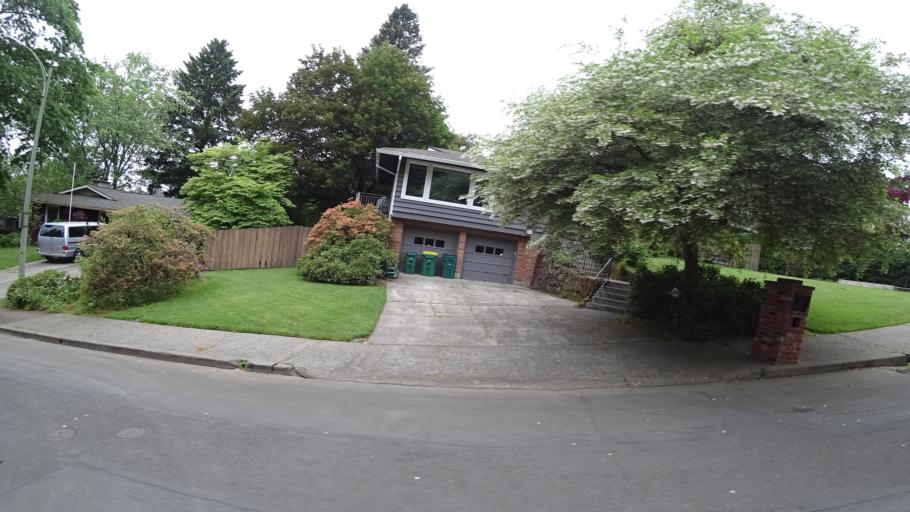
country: US
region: Oregon
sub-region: Washington County
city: Raleigh Hills
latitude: 45.4796
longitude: -122.7446
